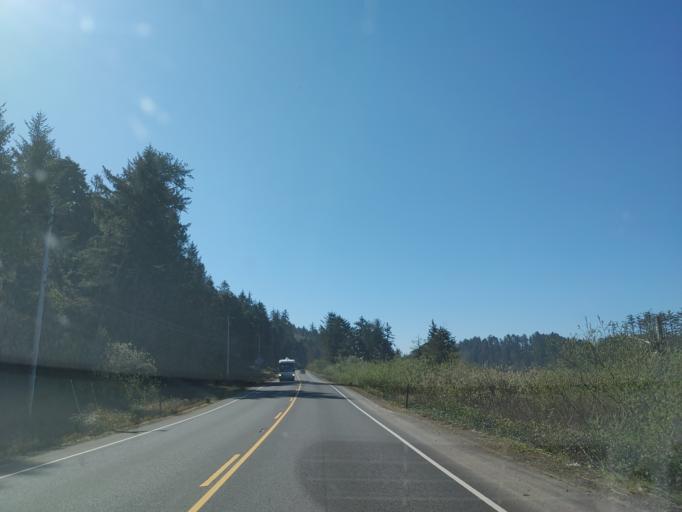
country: US
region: Oregon
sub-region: Tillamook County
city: Rockaway Beach
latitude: 45.5851
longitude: -123.9472
